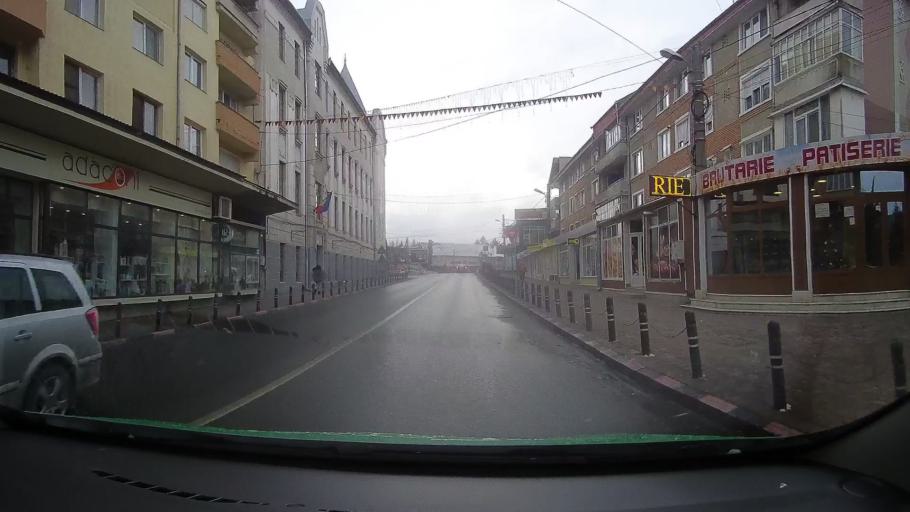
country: RO
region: Hunedoara
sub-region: Oras Hateg
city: Hateg
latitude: 45.6093
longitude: 22.9492
